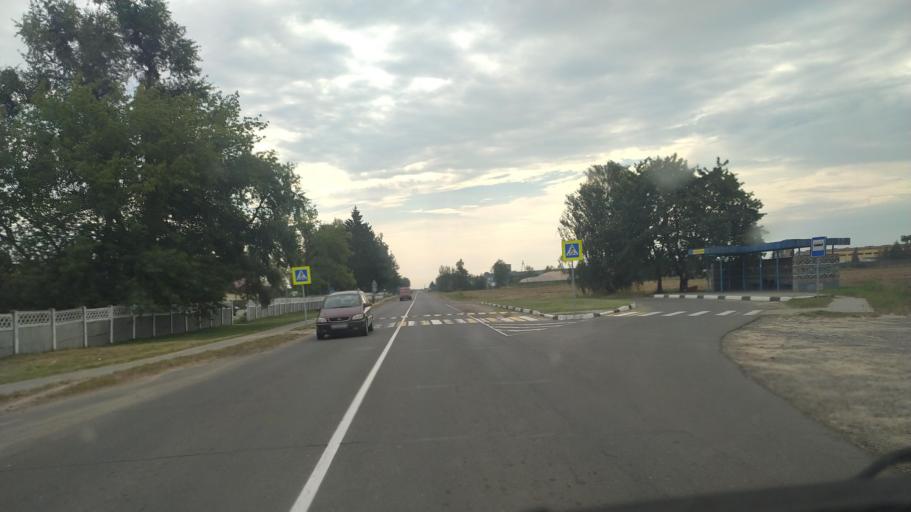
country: BY
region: Brest
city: Byaroza
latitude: 52.5544
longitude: 24.9252
